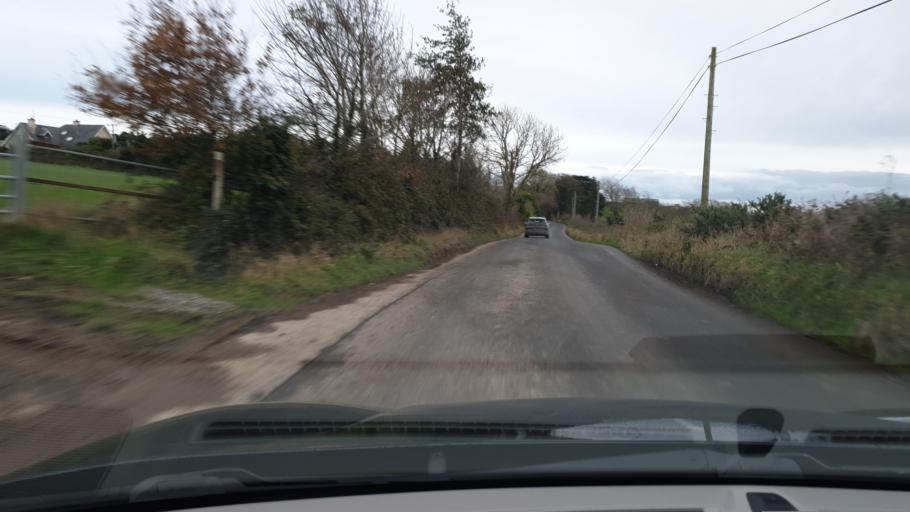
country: IE
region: Leinster
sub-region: An Mhi
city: Stamullin
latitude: 53.5581
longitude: -6.2648
